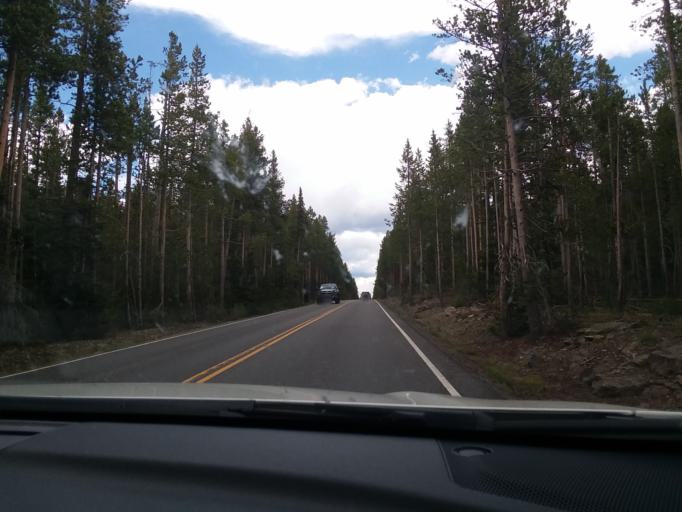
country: US
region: Idaho
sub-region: Teton County
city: Driggs
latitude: 44.1723
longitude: -110.6624
